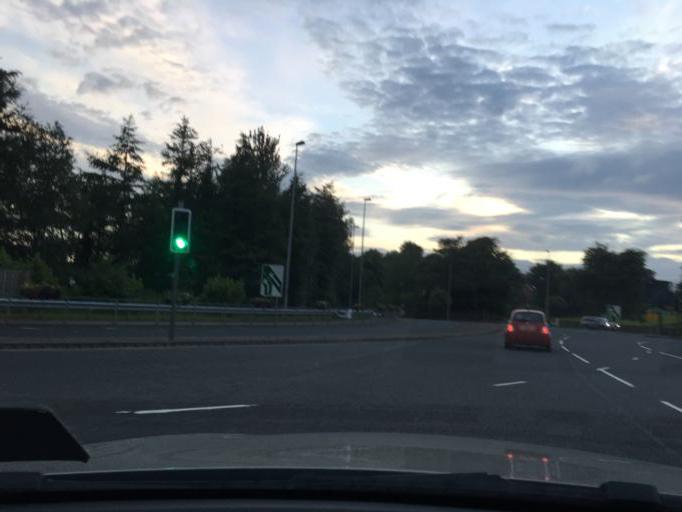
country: GB
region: Northern Ireland
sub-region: City of Derry
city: Derry
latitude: 55.0233
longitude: -7.3036
